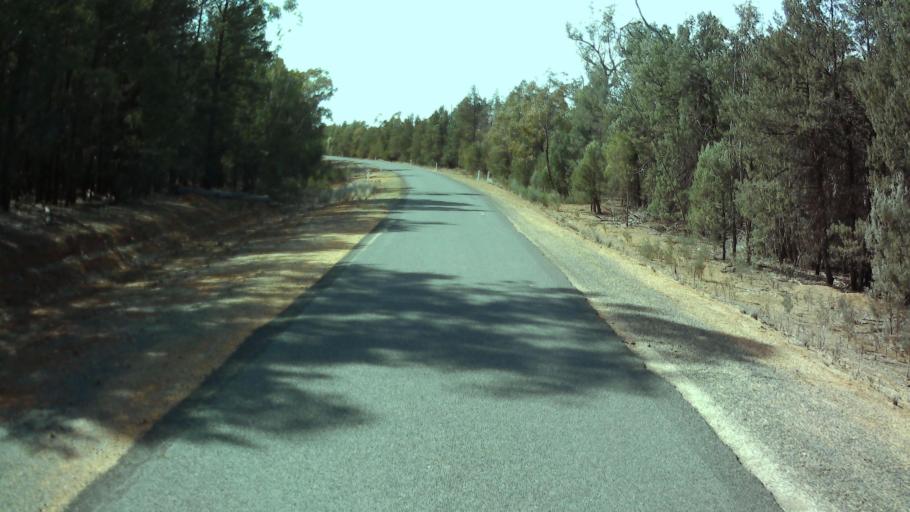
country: AU
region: New South Wales
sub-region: Weddin
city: Grenfell
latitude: -33.7365
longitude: 148.0416
